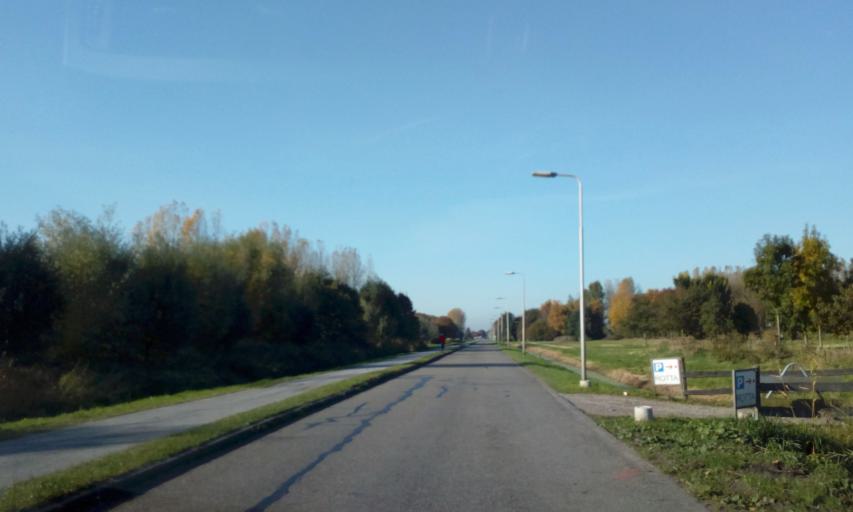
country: NL
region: South Holland
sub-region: Gemeente Lansingerland
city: Bleiswijk
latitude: 51.9725
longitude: 4.5350
